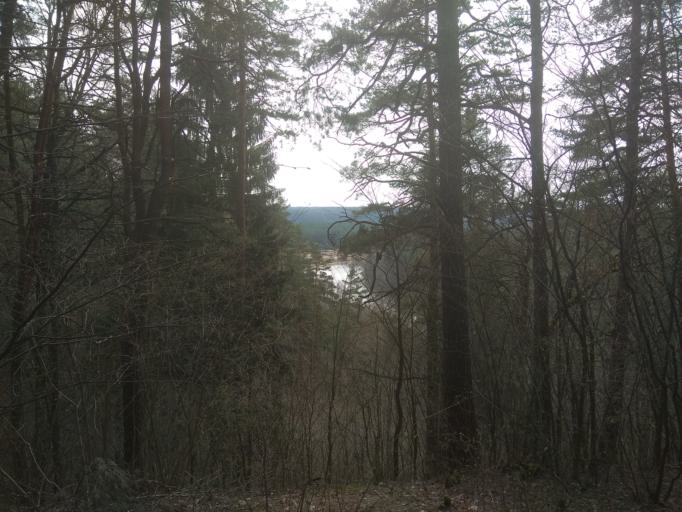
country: LT
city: Grigiskes
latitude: 54.7385
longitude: 25.0242
